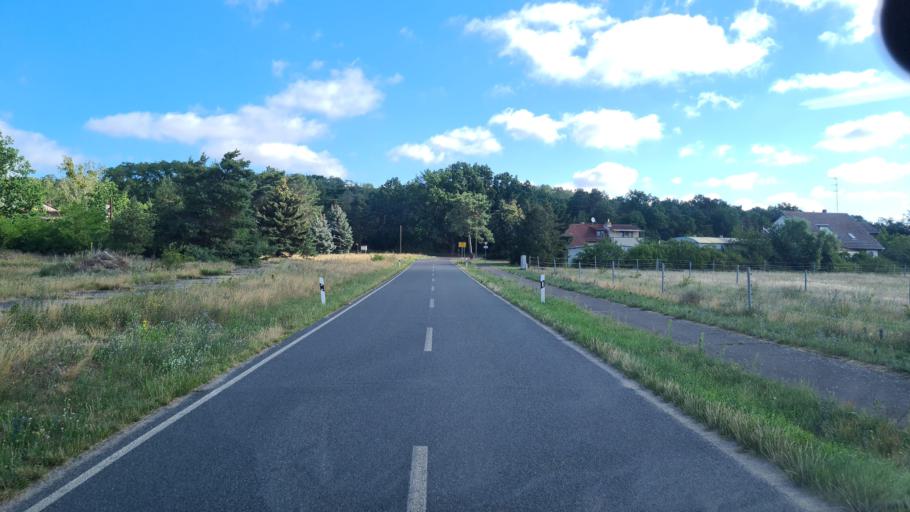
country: DE
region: Brandenburg
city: Trebbin
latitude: 52.2392
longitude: 13.1577
